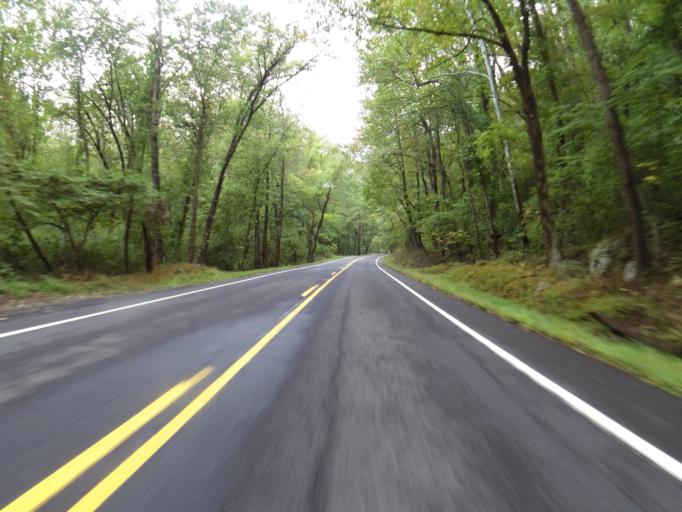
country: US
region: Virginia
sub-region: Rappahannock County
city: Washington
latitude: 38.6585
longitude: -78.2820
